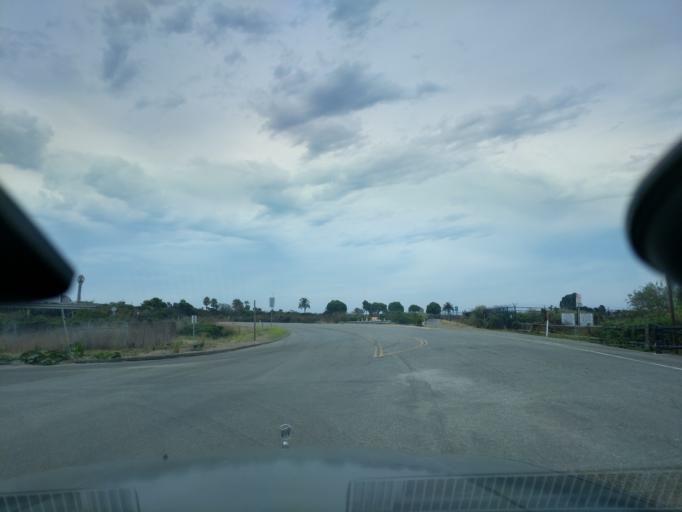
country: US
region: California
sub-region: Santa Barbara County
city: Goleta
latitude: 34.4194
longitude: -119.8352
